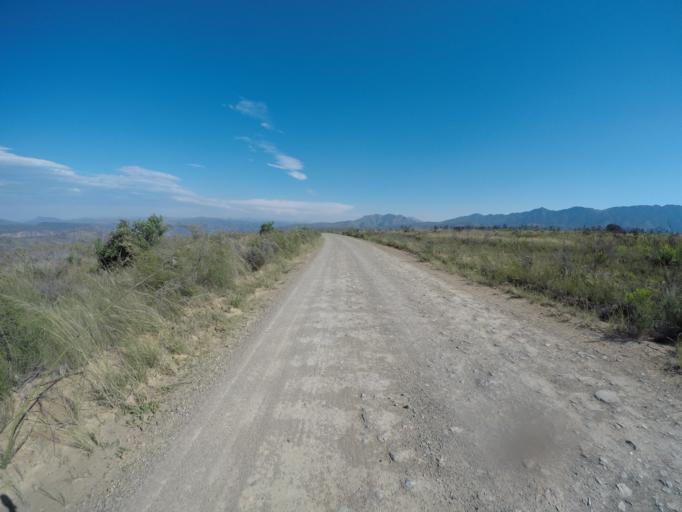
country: ZA
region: Eastern Cape
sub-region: Cacadu District Municipality
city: Kareedouw
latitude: -33.6340
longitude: 24.4794
